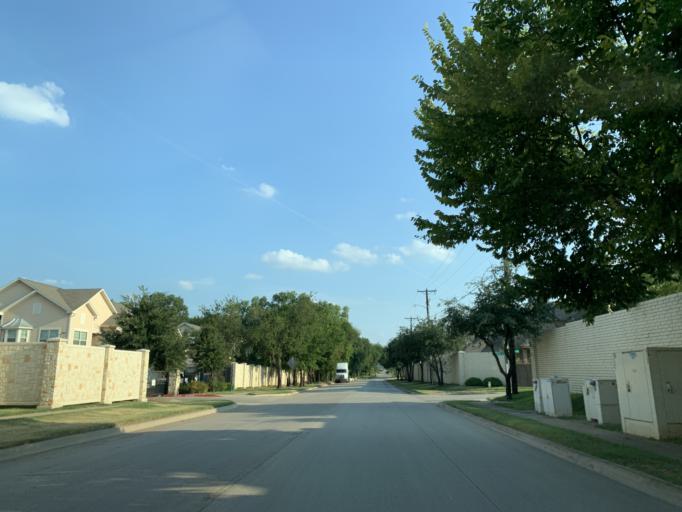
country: US
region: Texas
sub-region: Tarrant County
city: Hurst
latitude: 32.8012
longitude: -97.1691
